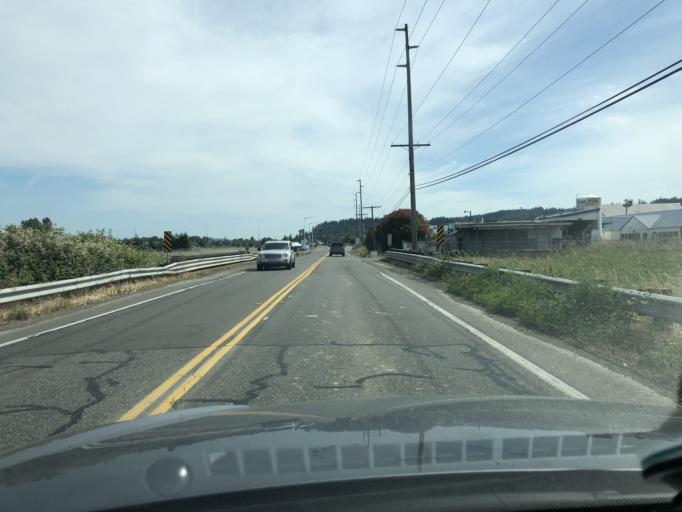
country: US
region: Washington
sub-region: King County
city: Kent
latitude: 47.3568
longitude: -122.2494
